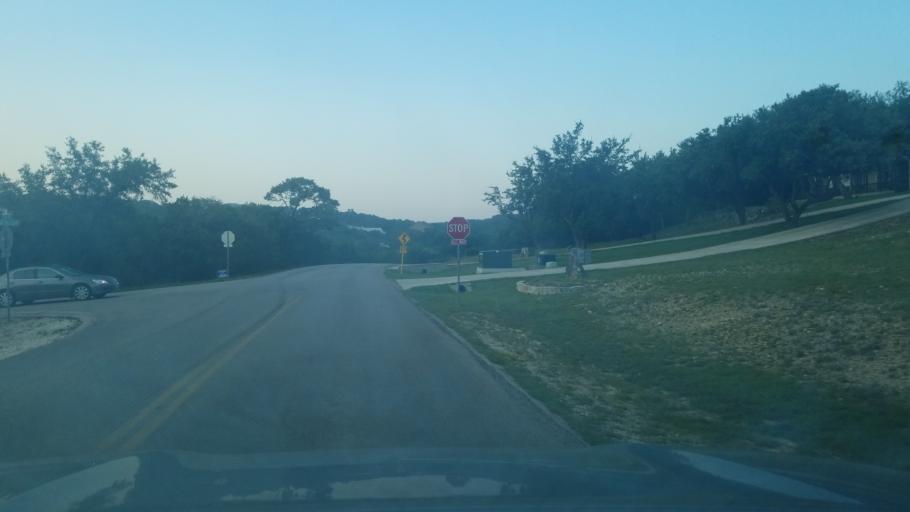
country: US
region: Texas
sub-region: Comal County
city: Bulverde
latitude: 29.8146
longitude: -98.4067
